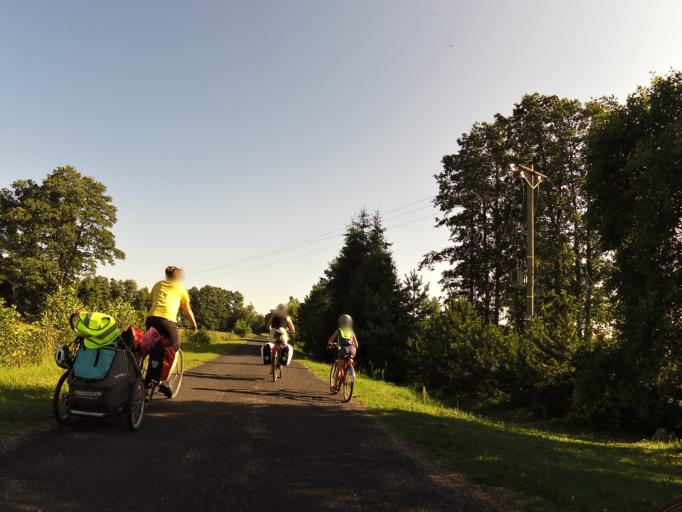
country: EE
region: Hiiumaa
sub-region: Kaerdla linn
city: Kardla
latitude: 58.7791
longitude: 22.4858
